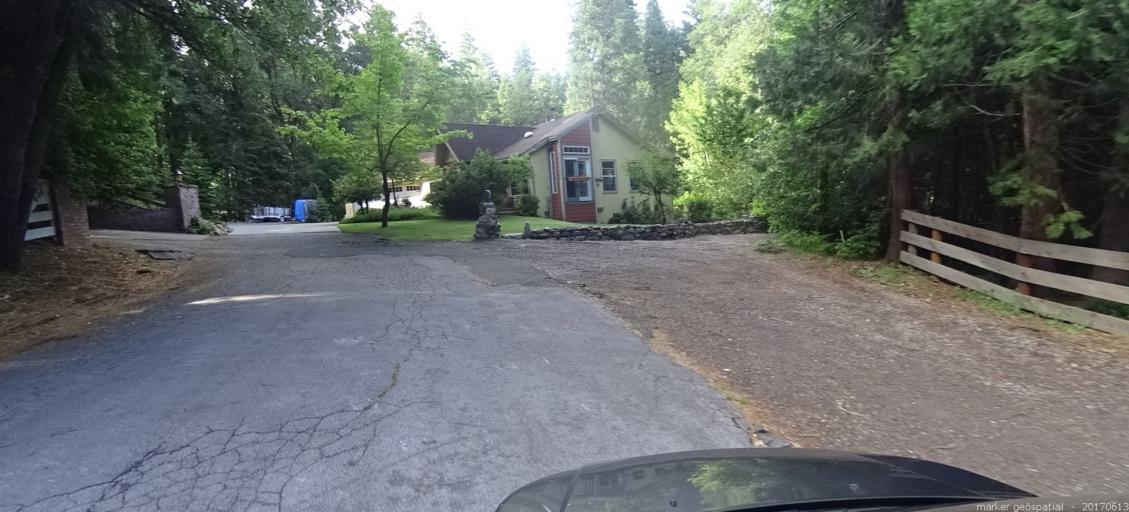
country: US
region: California
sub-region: Siskiyou County
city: Mount Shasta
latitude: 41.3110
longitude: -122.3042
